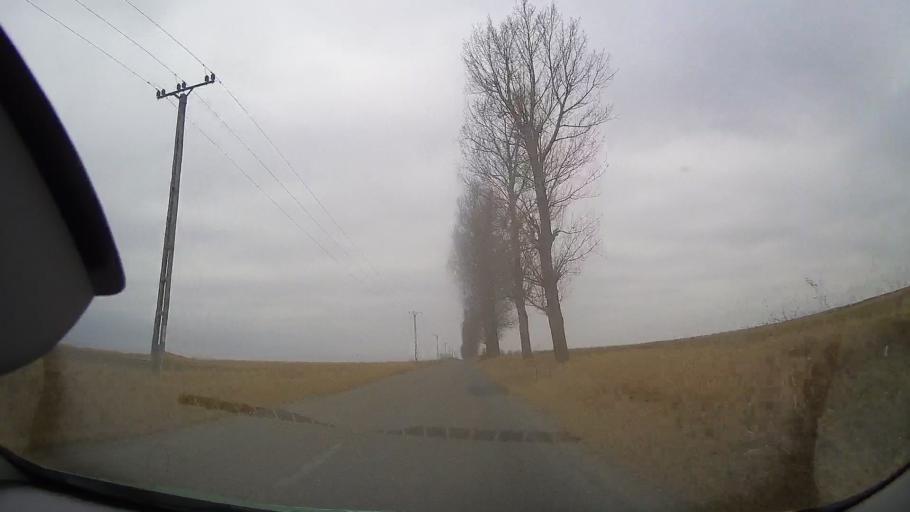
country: RO
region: Buzau
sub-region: Comuna Pogoanele
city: Pogoanele
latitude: 44.9621
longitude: 27.0213
